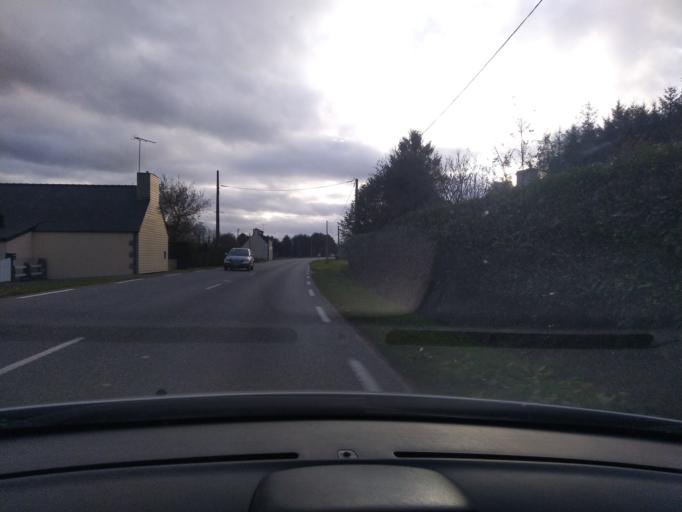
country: FR
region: Brittany
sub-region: Departement des Cotes-d'Armor
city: Plouaret
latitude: 48.5968
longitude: -3.4921
